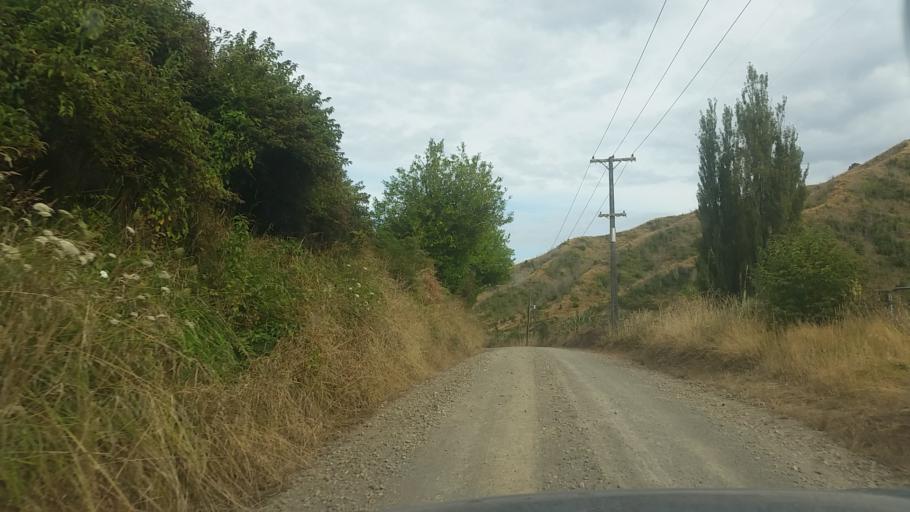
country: NZ
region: Taranaki
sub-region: New Plymouth District
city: Waitara
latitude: -39.1360
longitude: 174.7116
